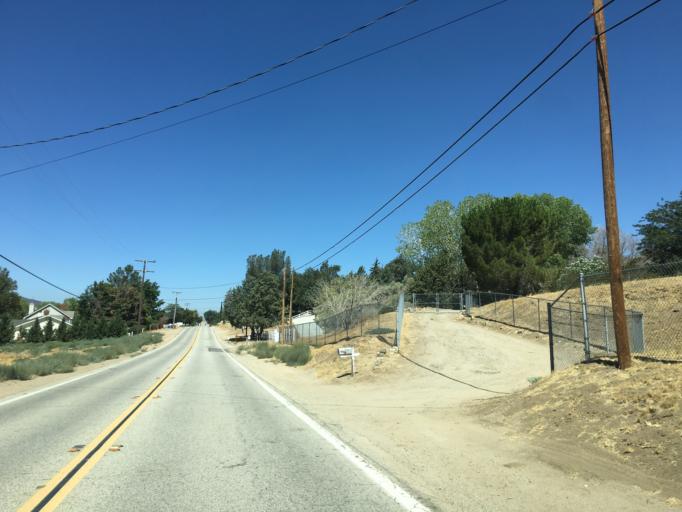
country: US
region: California
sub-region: Los Angeles County
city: Leona Valley
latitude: 34.6154
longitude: -118.2810
